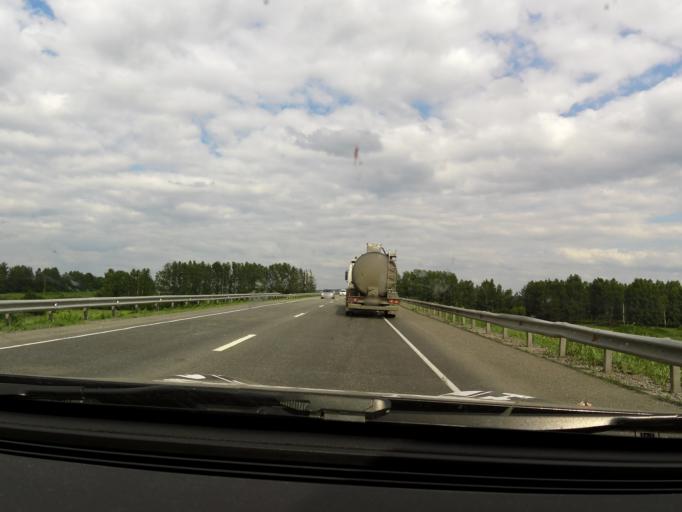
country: RU
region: Sverdlovsk
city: Druzhinino
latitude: 56.8108
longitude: 59.5114
